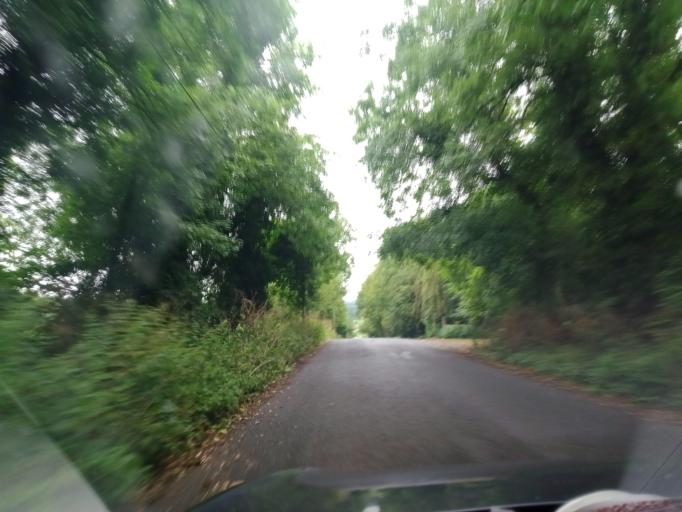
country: IE
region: Leinster
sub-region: Laois
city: Abbeyleix
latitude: 52.9213
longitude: -7.2843
